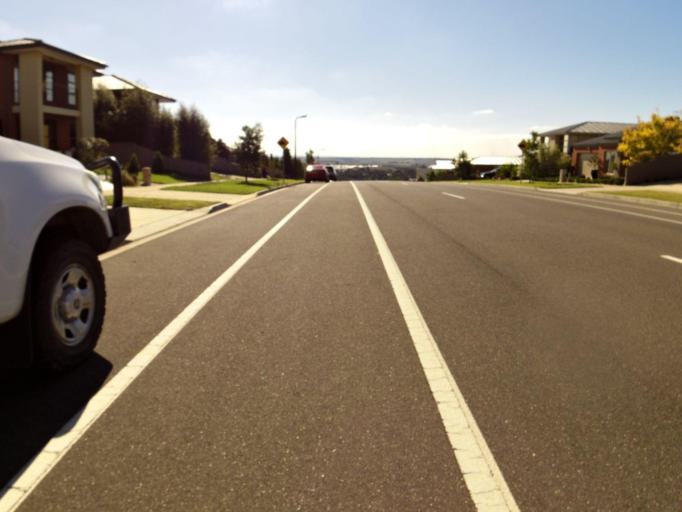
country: AU
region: Victoria
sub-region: Greater Geelong
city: Wandana Heights
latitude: -38.1568
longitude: 144.2988
